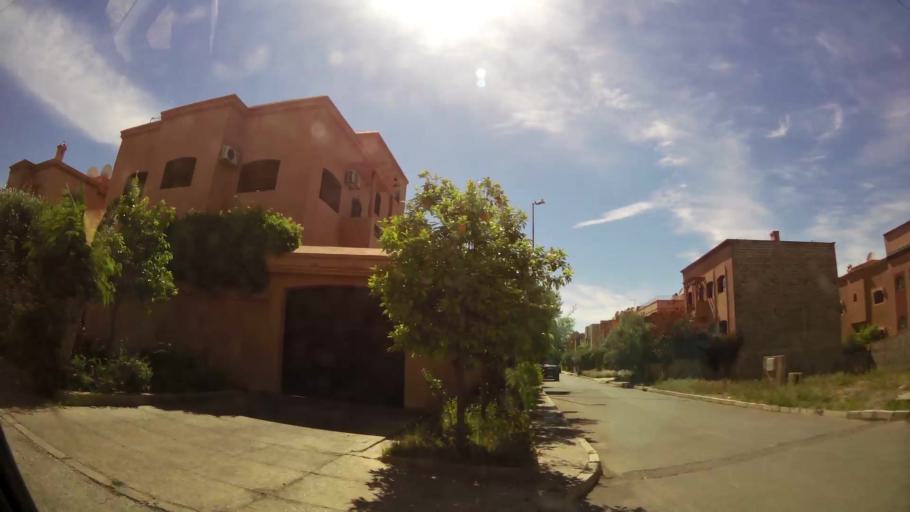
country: MA
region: Marrakech-Tensift-Al Haouz
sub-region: Marrakech
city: Marrakesh
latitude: 31.6804
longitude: -8.0039
